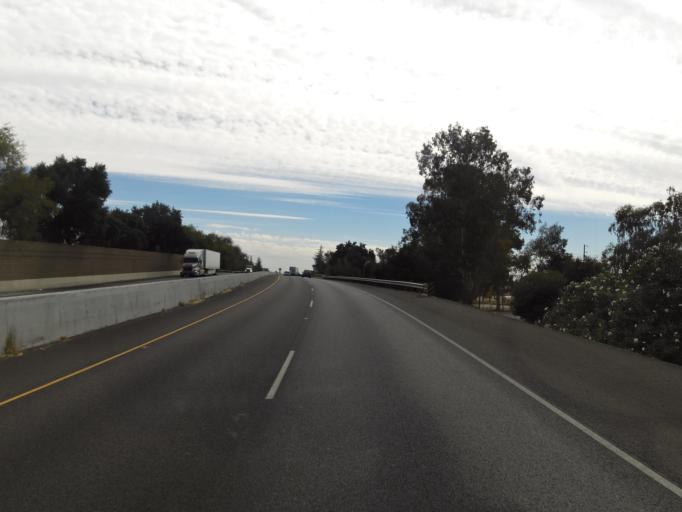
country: US
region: California
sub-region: Colusa County
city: Arbuckle
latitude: 39.0141
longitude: -122.0568
